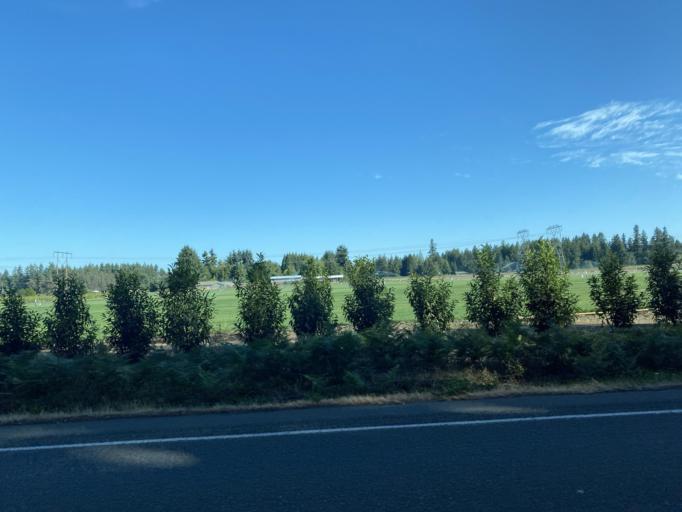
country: US
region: Washington
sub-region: Thurston County
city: Tanglewilde-Thompson Place
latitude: 46.9788
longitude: -122.7680
